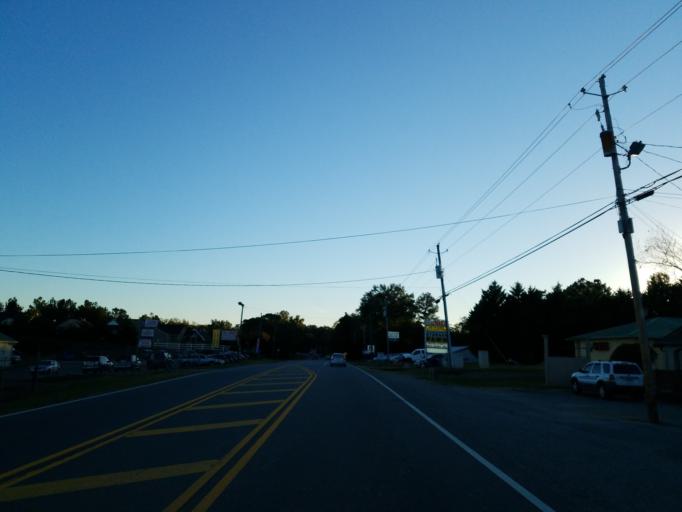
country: US
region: Georgia
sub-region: Forsyth County
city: Cumming
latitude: 34.2394
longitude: -84.1209
